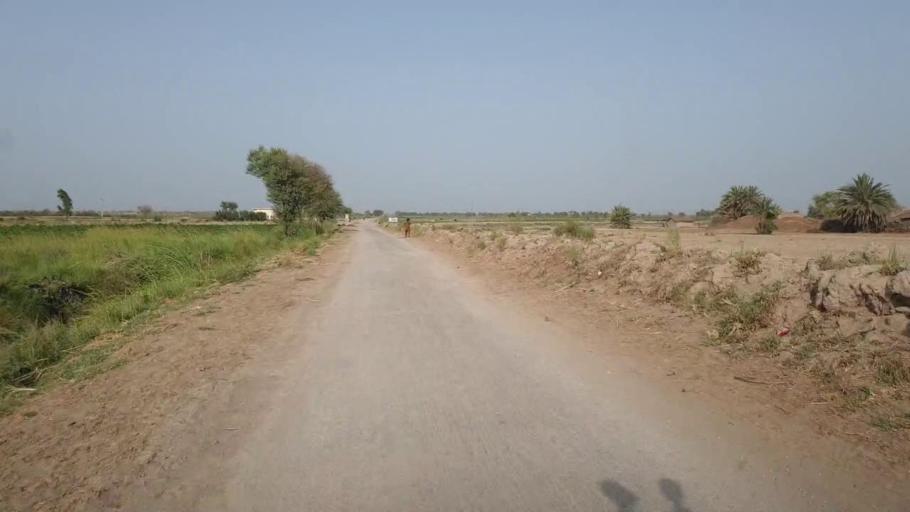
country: PK
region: Sindh
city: Daur
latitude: 26.3405
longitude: 68.2080
